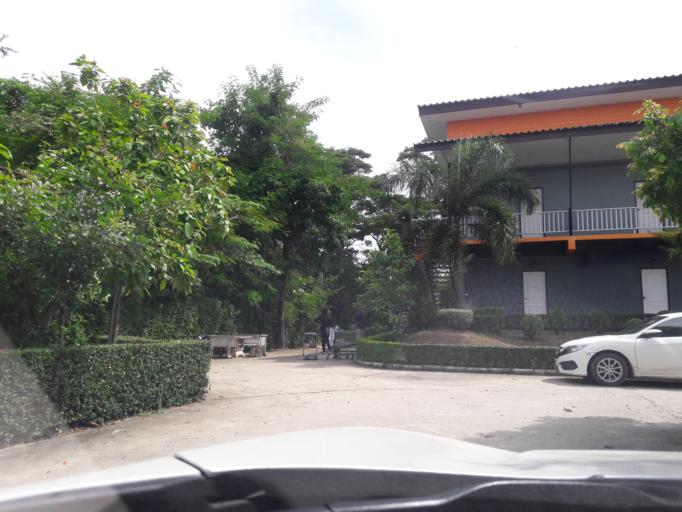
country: TH
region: Lop Buri
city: Ban Mi
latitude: 15.0445
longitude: 100.5574
